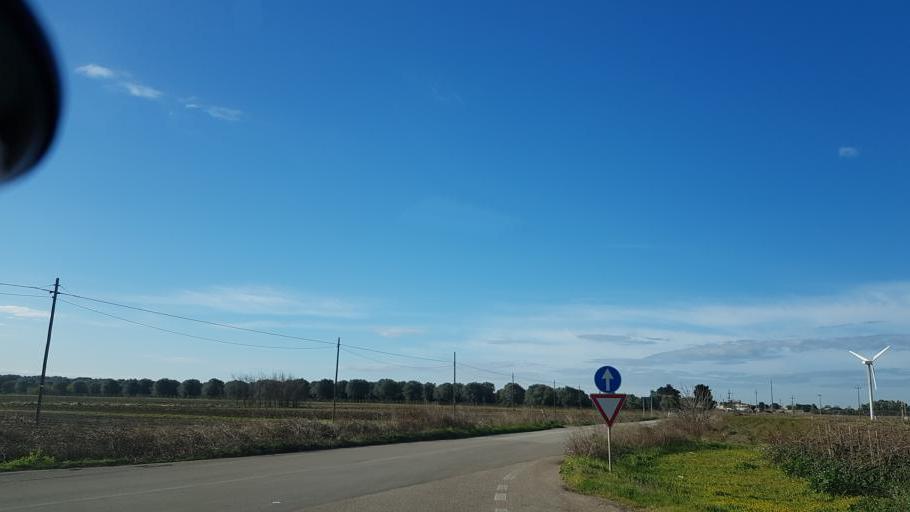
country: IT
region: Apulia
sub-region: Provincia di Brindisi
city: Tuturano
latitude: 40.5533
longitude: 17.9922
